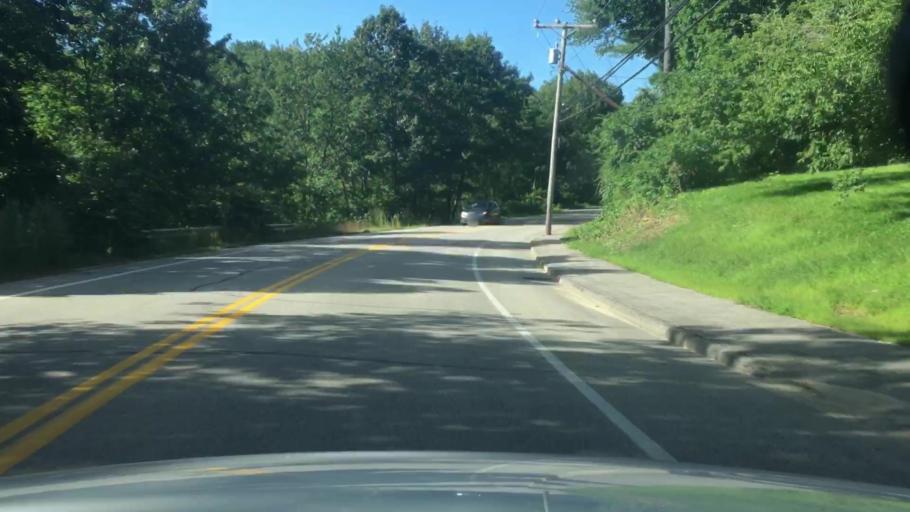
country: US
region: New Hampshire
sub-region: Strafford County
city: Dover
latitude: 43.1701
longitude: -70.8729
